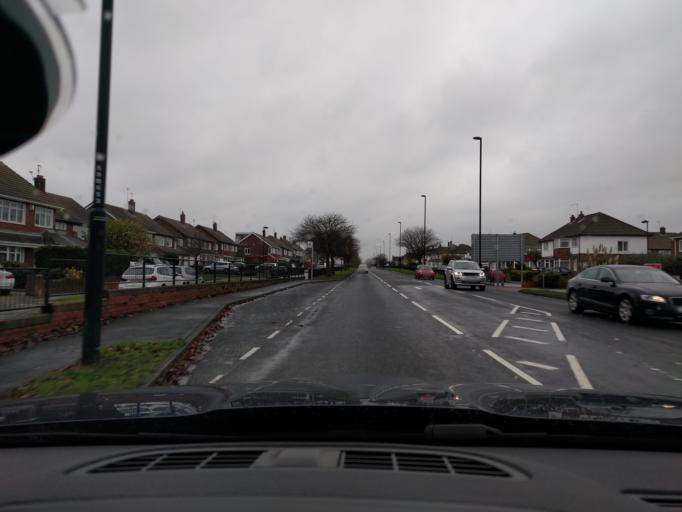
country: GB
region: England
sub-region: Borough of North Tyneside
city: Tynemouth
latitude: 55.0250
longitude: -1.4361
